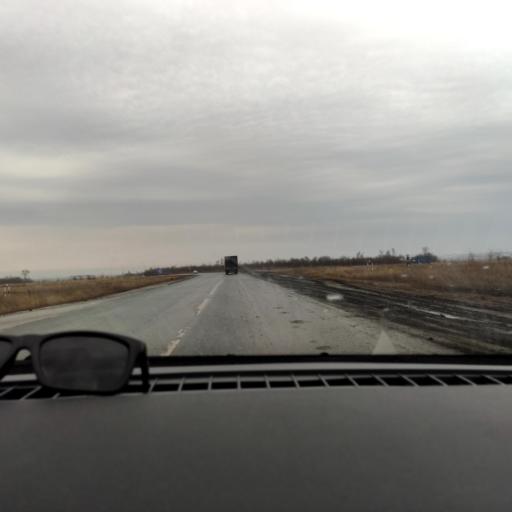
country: RU
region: Samara
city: Smyshlyayevka
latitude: 53.1405
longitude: 50.3834
